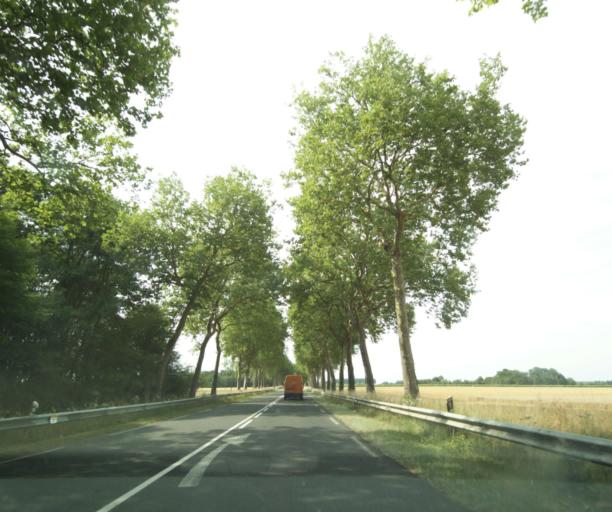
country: FR
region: Centre
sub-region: Departement d'Indre-et-Loire
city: Neuille-Pont-Pierre
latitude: 47.5330
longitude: 0.5639
